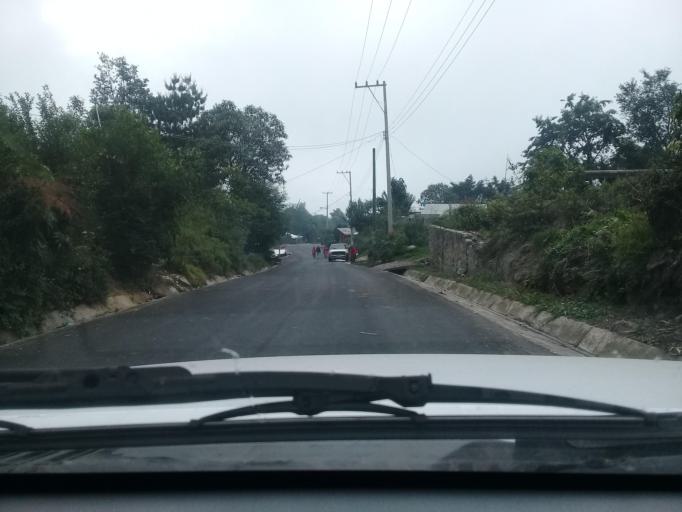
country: MX
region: Veracruz
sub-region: Mariano Escobedo
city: San Isidro el Berro
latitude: 18.9491
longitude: -97.2073
